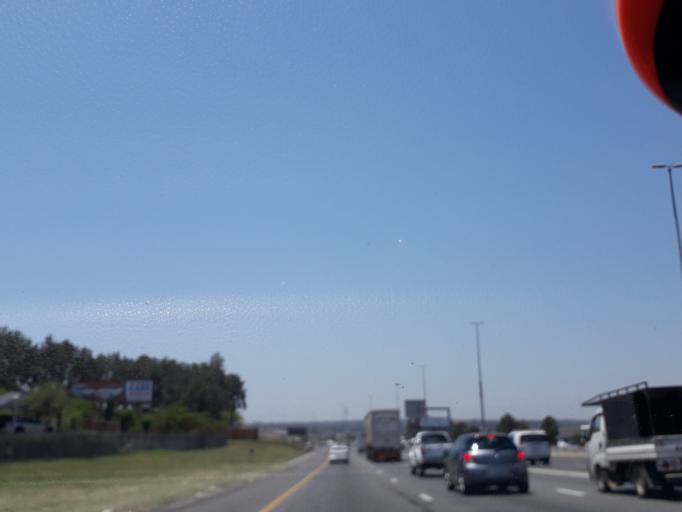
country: ZA
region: Gauteng
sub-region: City of Johannesburg Metropolitan Municipality
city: Midrand
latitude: -26.0428
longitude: 28.1018
